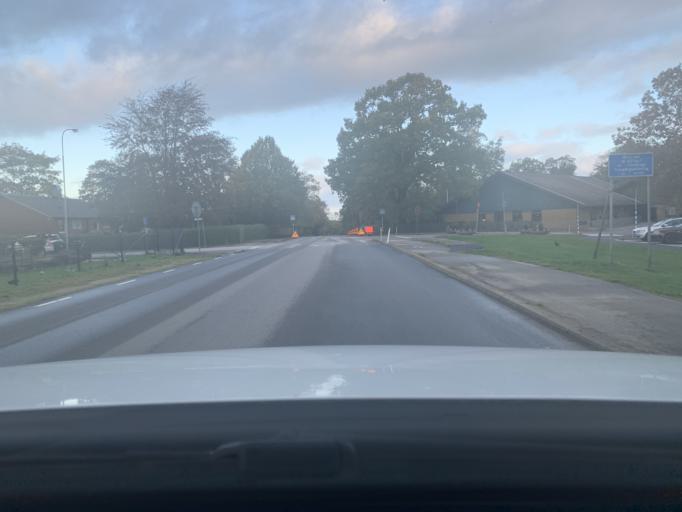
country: SE
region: Skane
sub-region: Horby Kommun
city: Hoerby
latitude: 55.8410
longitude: 13.6571
